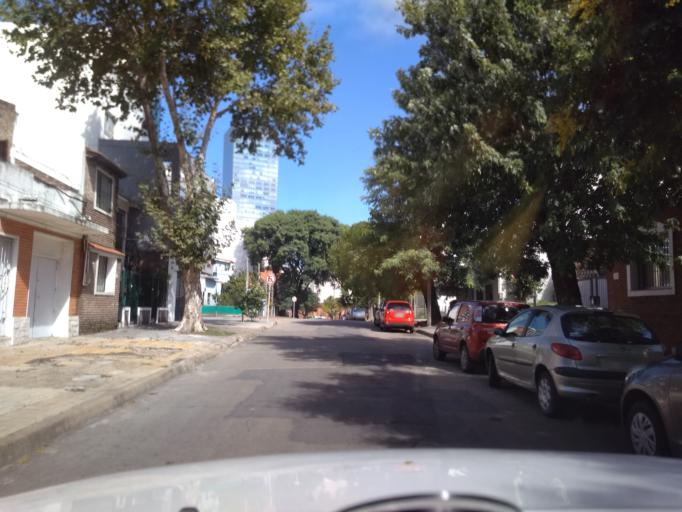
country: UY
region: Montevideo
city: Montevideo
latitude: -34.9009
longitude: -56.1367
